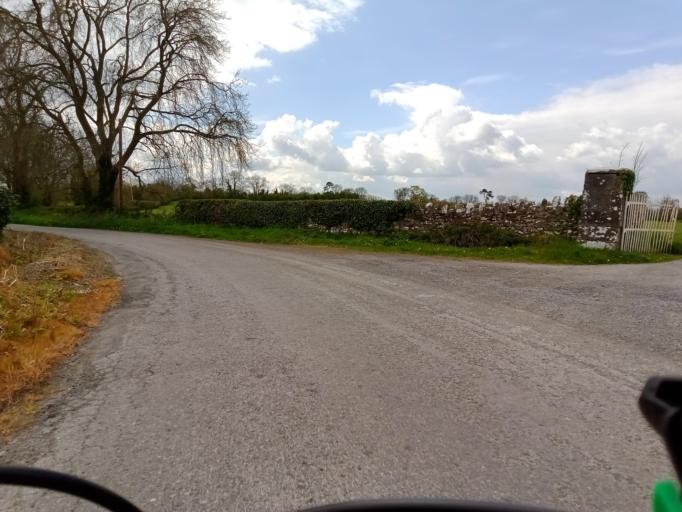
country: IE
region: Leinster
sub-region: Kilkenny
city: Kilkenny
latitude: 52.6340
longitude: -7.2816
